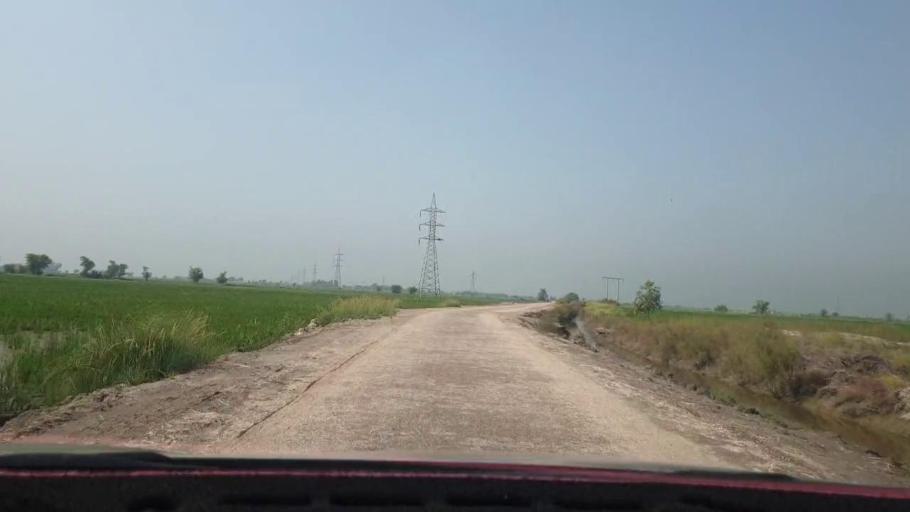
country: PK
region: Sindh
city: Nasirabad
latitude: 27.4281
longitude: 67.9447
